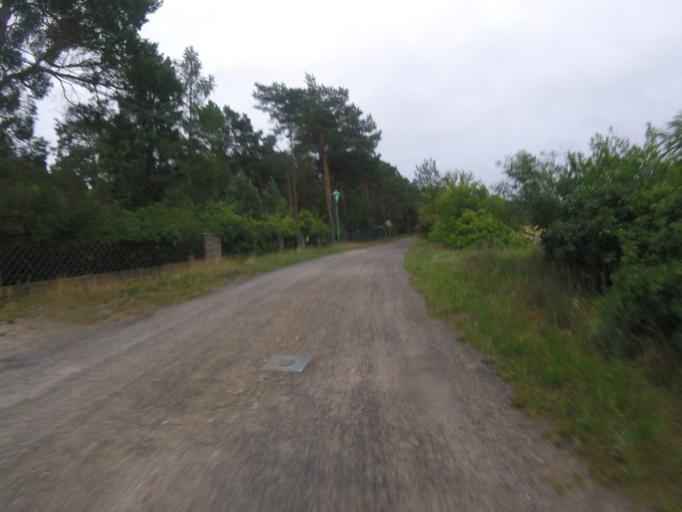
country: DE
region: Brandenburg
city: Bestensee
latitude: 52.2345
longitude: 13.7212
